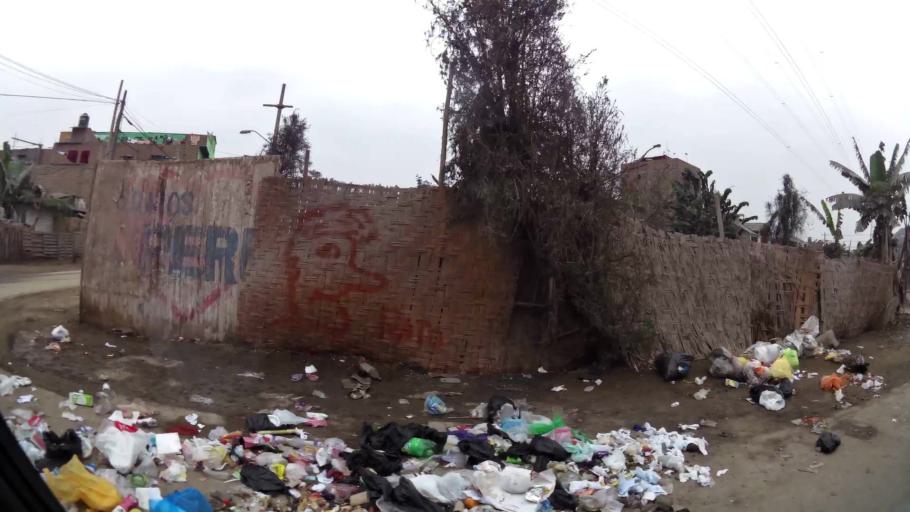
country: PE
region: Lima
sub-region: Lima
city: Urb. Santo Domingo
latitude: -11.9008
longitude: -77.0667
